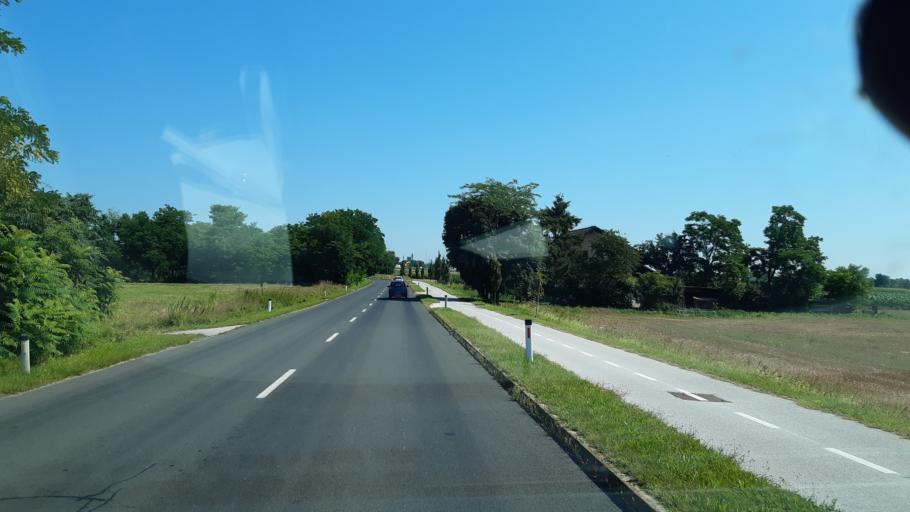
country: SI
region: Murska Sobota
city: Bakovci
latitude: 46.6314
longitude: 16.1573
